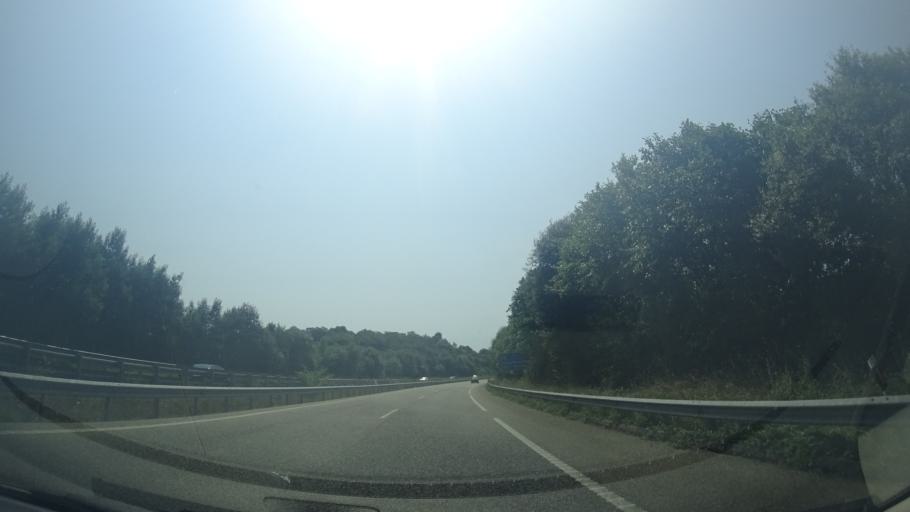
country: ES
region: Asturias
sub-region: Province of Asturias
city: Pola de Siero
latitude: 43.3709
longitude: -5.6819
